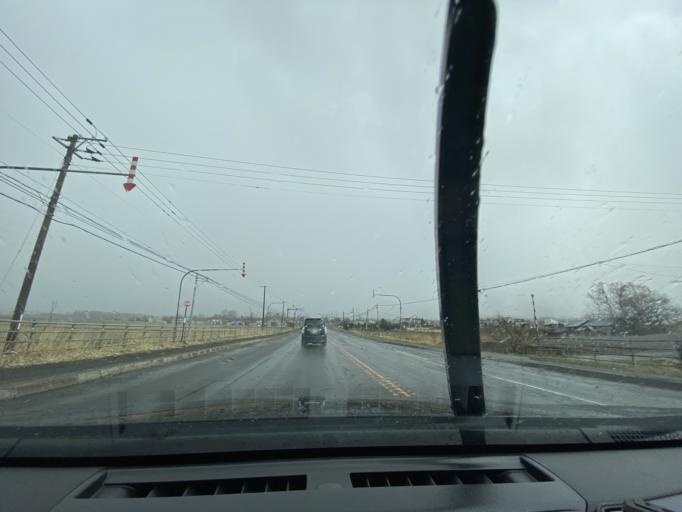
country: JP
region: Hokkaido
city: Takikawa
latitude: 43.6146
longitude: 141.9358
